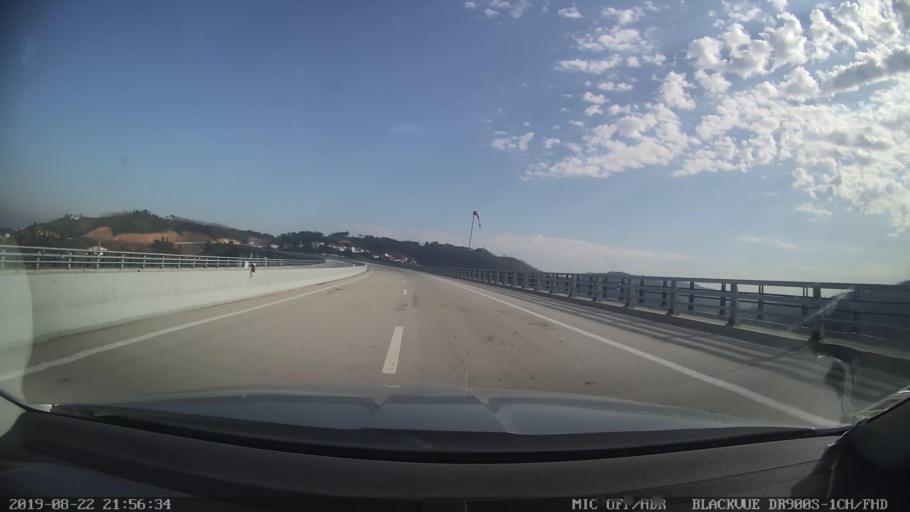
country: PT
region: Coimbra
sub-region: Coimbra
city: Coimbra
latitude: 40.1724
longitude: -8.3771
